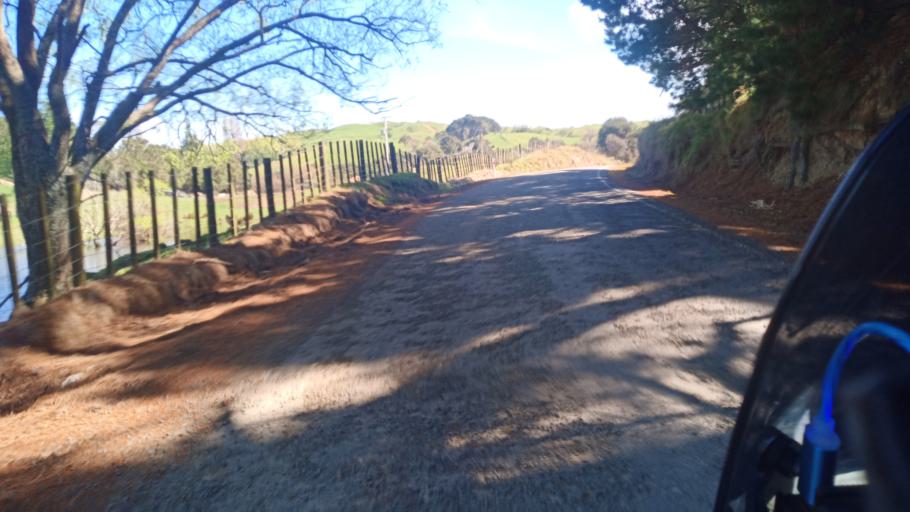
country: NZ
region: Gisborne
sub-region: Gisborne District
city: Gisborne
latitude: -37.9999
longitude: 178.3156
